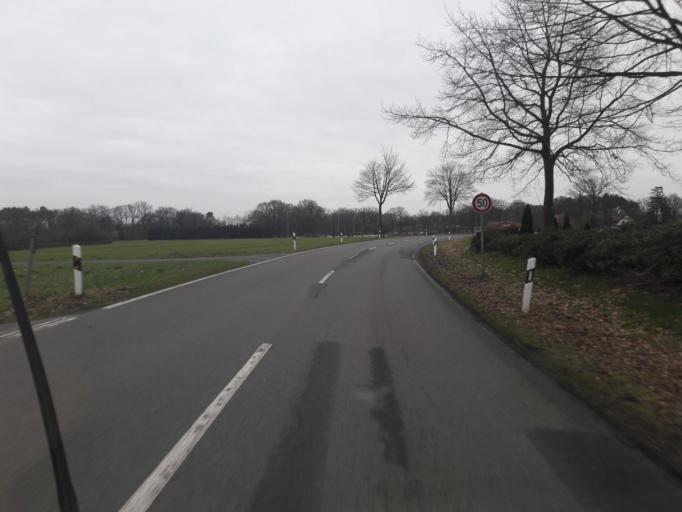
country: DE
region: Lower Saxony
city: Warmsen
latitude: 52.4250
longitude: 8.8557
